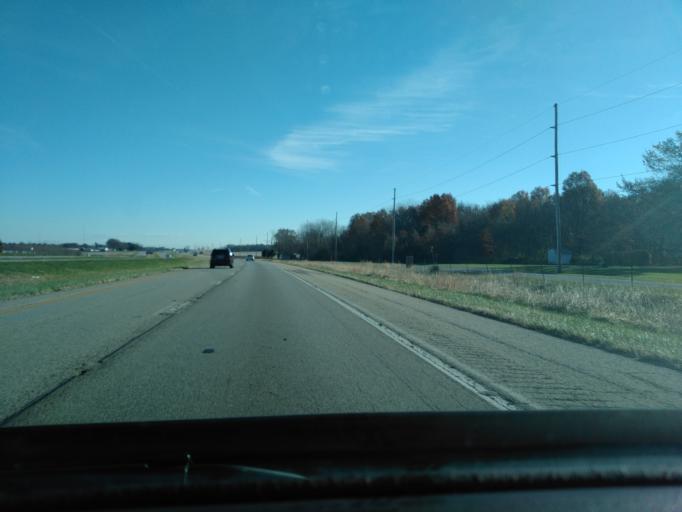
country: US
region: Illinois
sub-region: Bond County
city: Greenville
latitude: 38.8471
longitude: -89.4721
